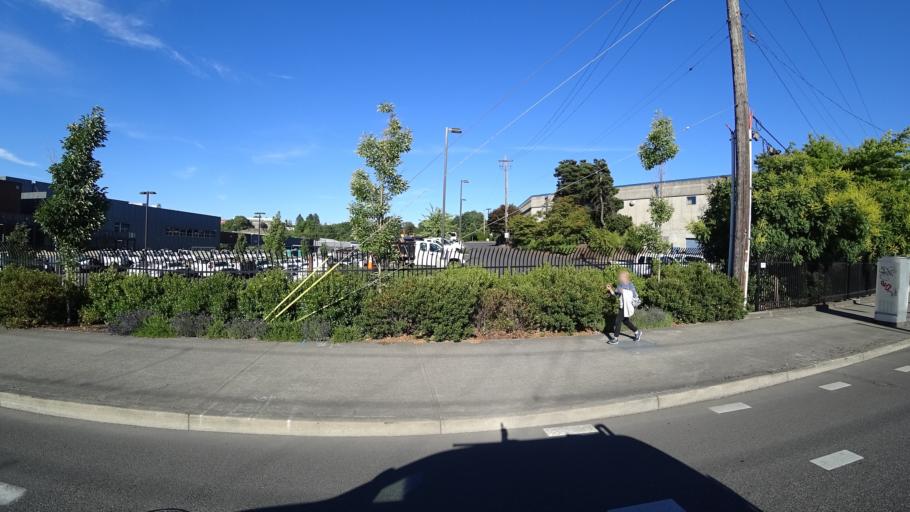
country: US
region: Oregon
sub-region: Multnomah County
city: Portland
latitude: 45.5366
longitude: -122.6744
